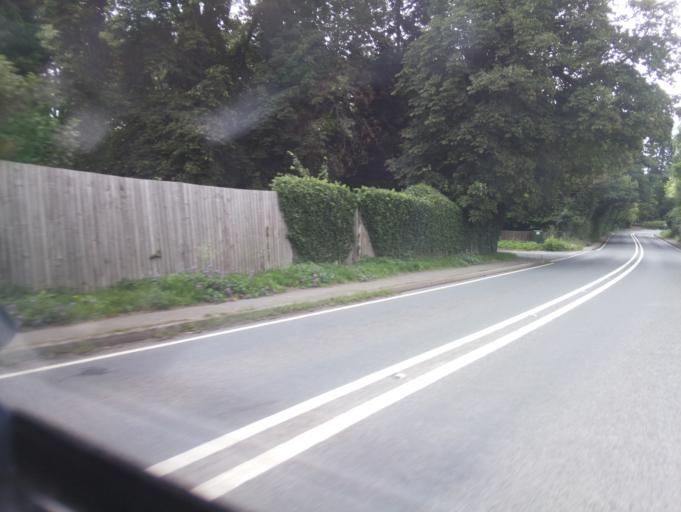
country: GB
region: England
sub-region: Worcestershire
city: Upton upon Severn
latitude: 52.0940
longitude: -2.2091
